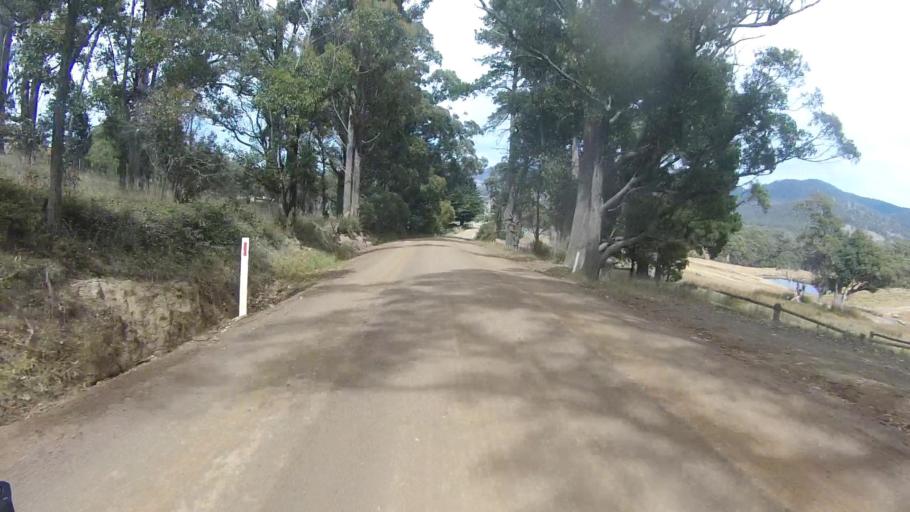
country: AU
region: Tasmania
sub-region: Sorell
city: Sorell
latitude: -42.7767
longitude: 147.8201
